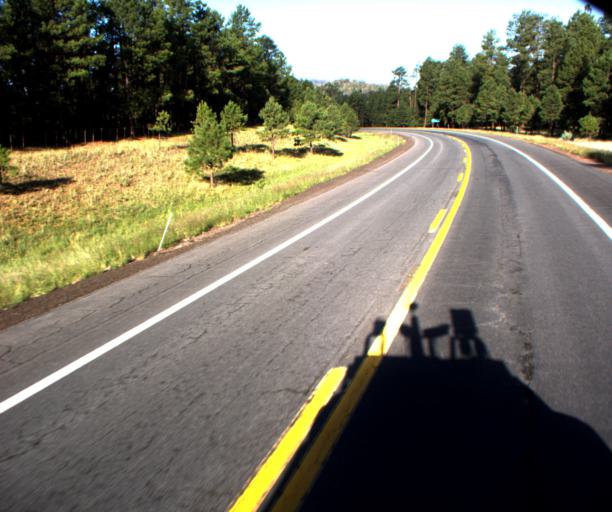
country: US
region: New Mexico
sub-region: Catron County
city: Reserve
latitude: 33.8133
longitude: -109.0584
